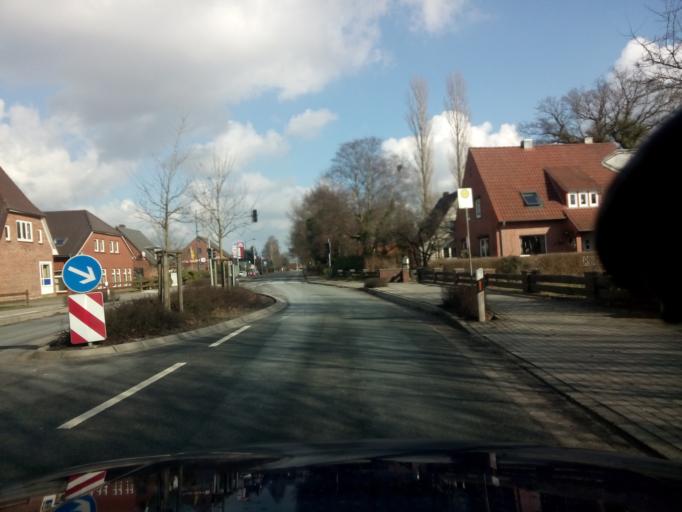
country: DE
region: Lower Saxony
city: Vollersode
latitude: 53.3223
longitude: 8.8864
